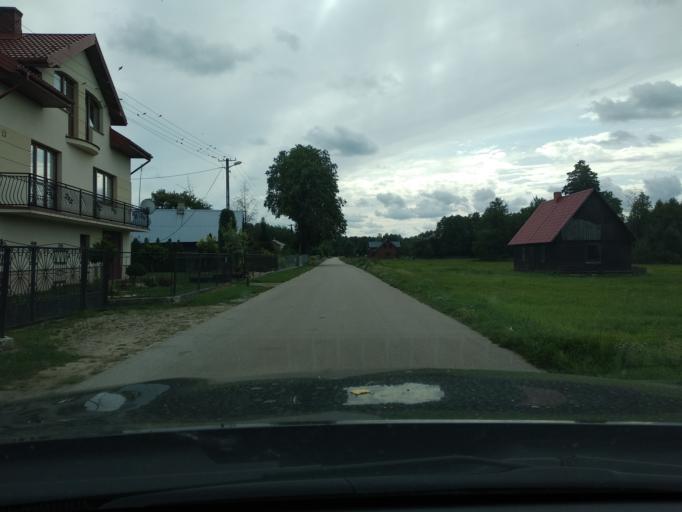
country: PL
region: Masovian Voivodeship
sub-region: Powiat pultuski
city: Obryte
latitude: 52.7317
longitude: 21.1645
